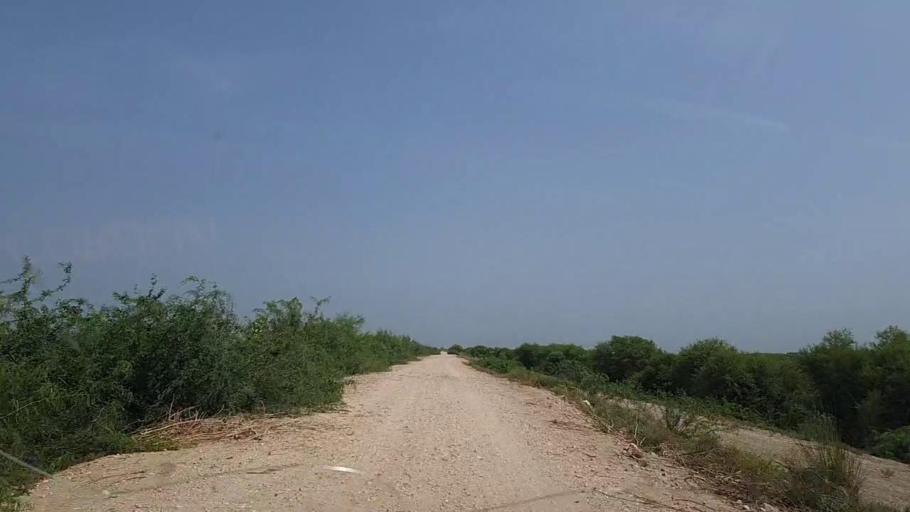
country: PK
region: Sindh
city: Ghotki
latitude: 28.1090
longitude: 69.3941
